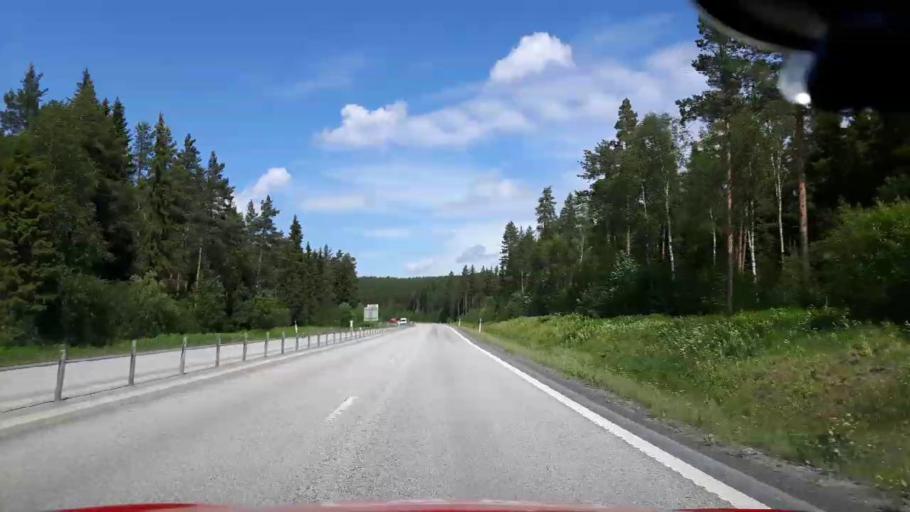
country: SE
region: Jaemtland
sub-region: OEstersunds Kommun
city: Ostersund
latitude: 63.1869
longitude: 14.6893
